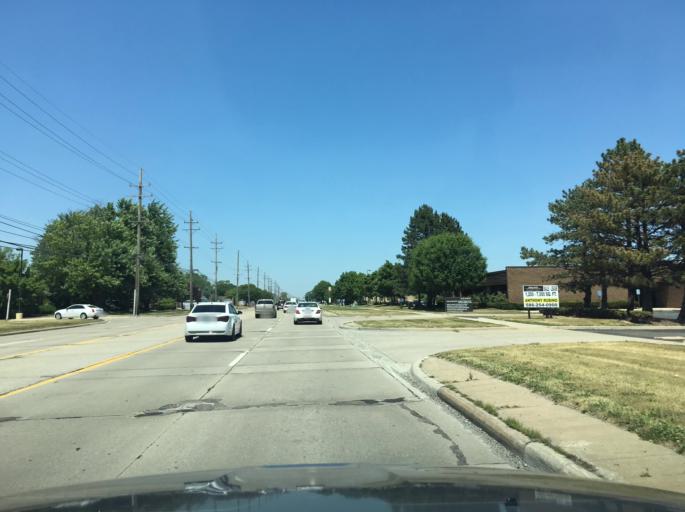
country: US
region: Michigan
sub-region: Macomb County
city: Clinton
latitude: 42.6082
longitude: -82.9527
